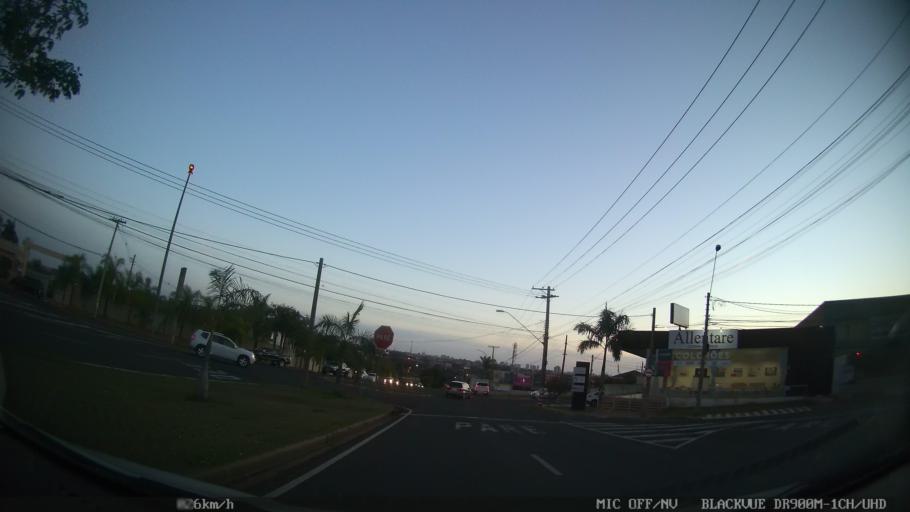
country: BR
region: Sao Paulo
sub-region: Sao Jose Do Rio Preto
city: Sao Jose do Rio Preto
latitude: -20.8080
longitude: -49.3491
